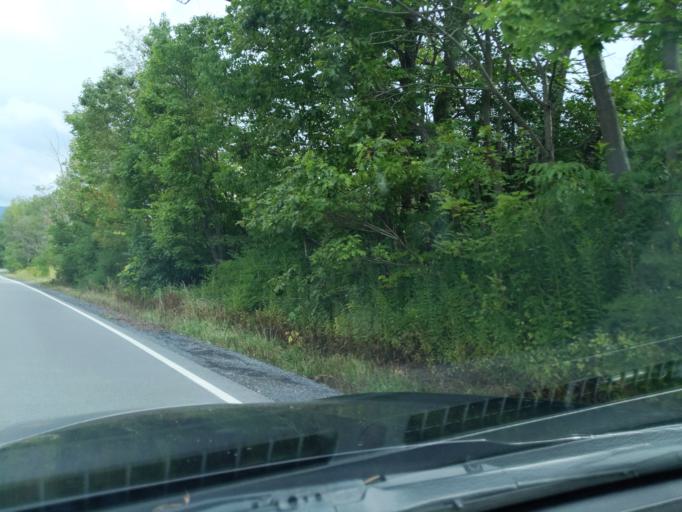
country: US
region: Pennsylvania
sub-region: Cambria County
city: Beaverdale
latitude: 40.2996
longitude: -78.5774
